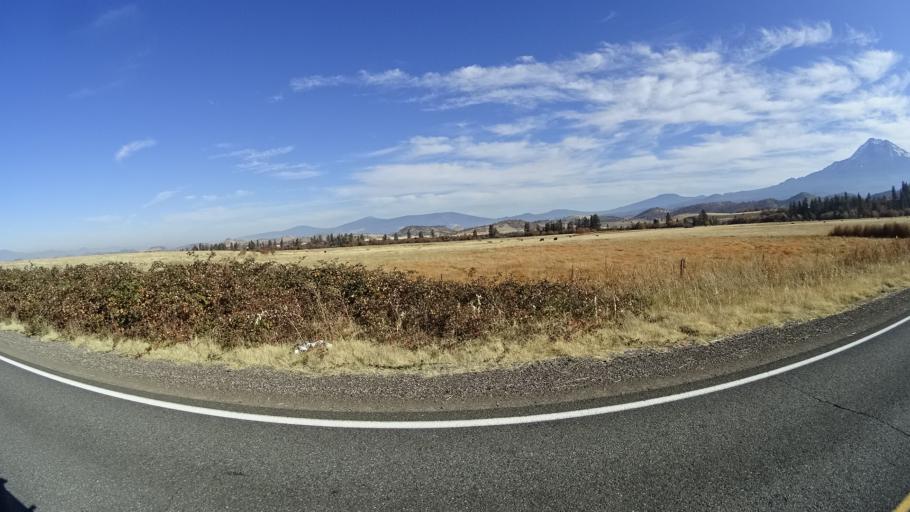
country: US
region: California
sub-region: Siskiyou County
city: Weed
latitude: 41.4523
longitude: -122.4566
